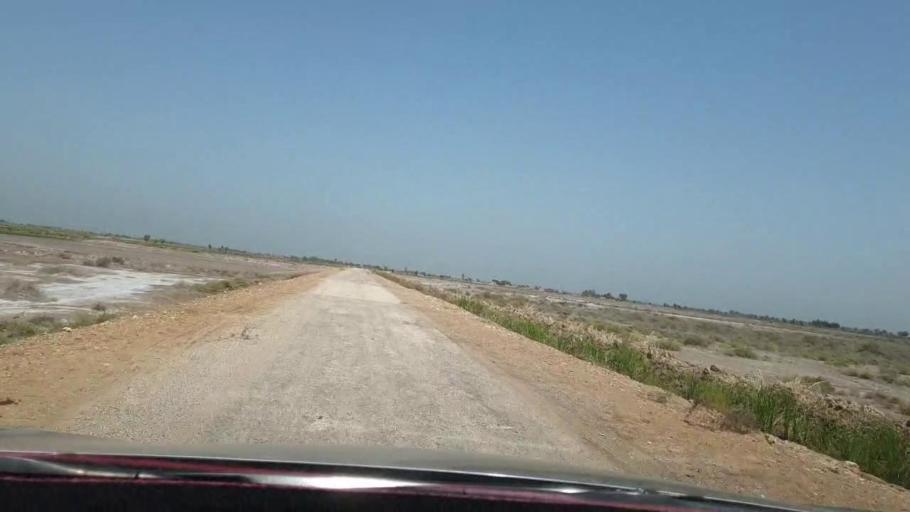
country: PK
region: Sindh
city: Warah
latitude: 27.5301
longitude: 67.7160
